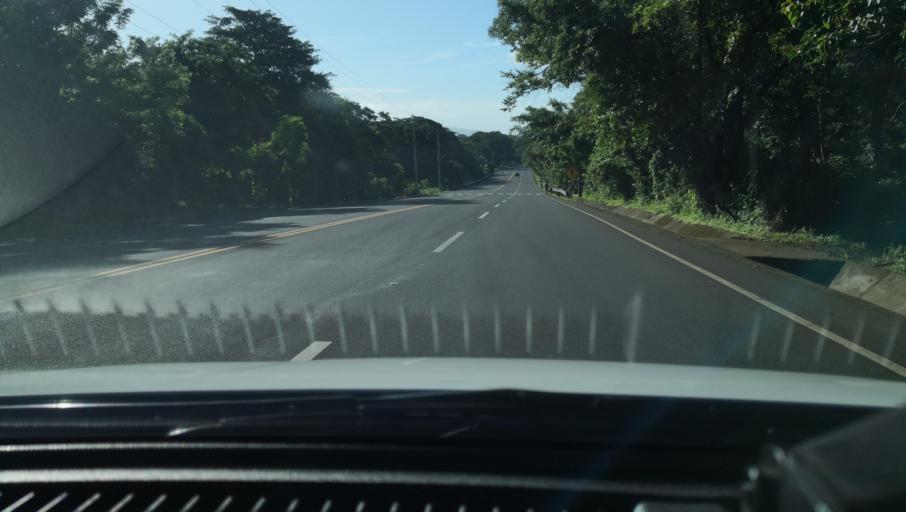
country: NI
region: Granada
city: Nandaime
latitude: 11.7892
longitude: -86.0630
